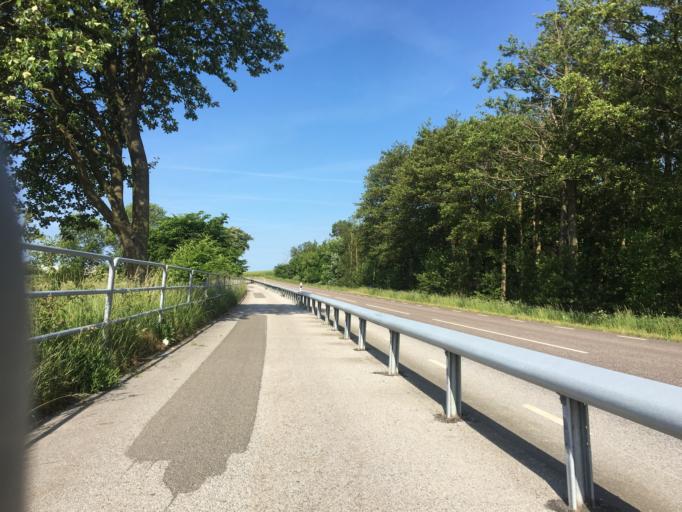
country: SE
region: Skane
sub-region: Skurups Kommun
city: Rydsgard
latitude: 55.4185
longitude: 13.6801
